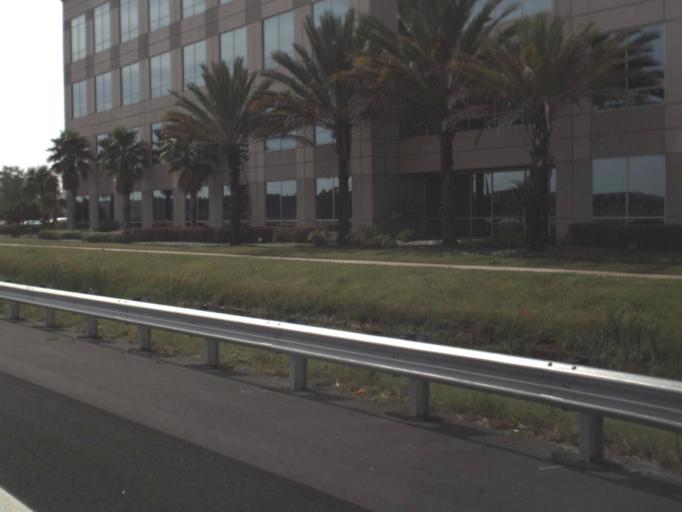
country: US
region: Florida
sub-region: Orange County
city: Williamsburg
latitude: 28.4352
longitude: -81.4244
